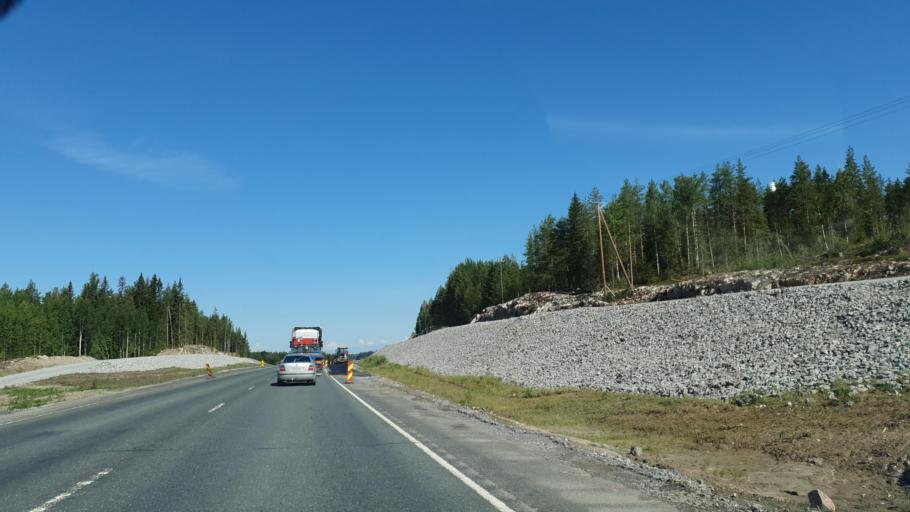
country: FI
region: Northern Savo
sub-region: Ylae-Savo
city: Lapinlahti
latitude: 63.2802
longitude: 27.4566
